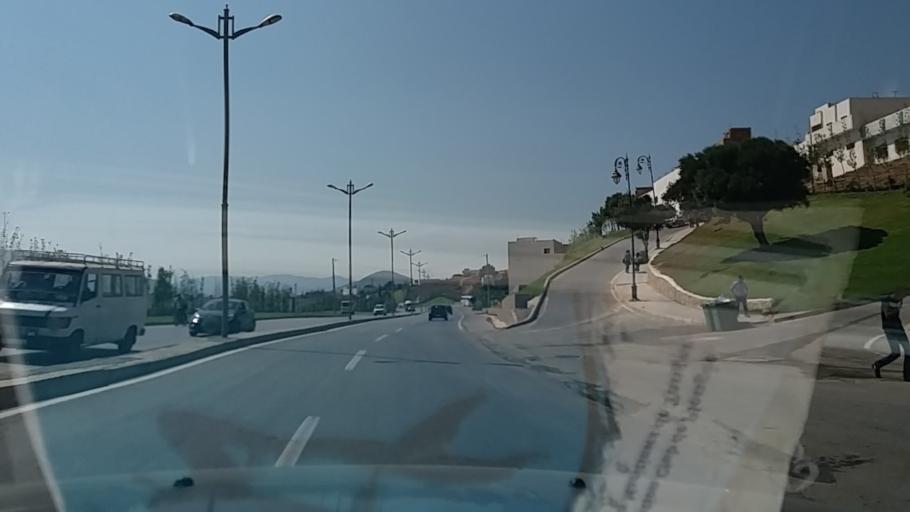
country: MA
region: Tanger-Tetouan
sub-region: Tetouan
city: Saddina
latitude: 35.5631
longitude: -5.4278
